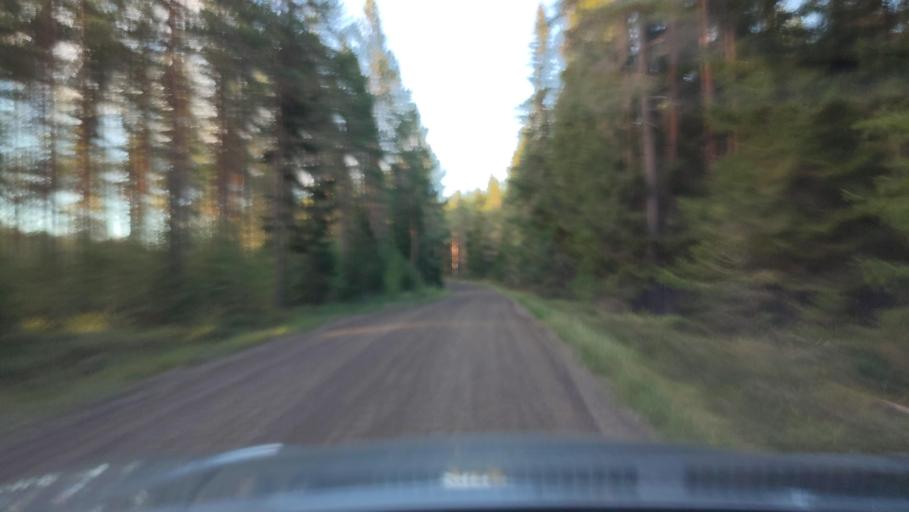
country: FI
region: Southern Ostrobothnia
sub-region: Suupohja
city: Karijoki
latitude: 62.2296
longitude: 21.5731
